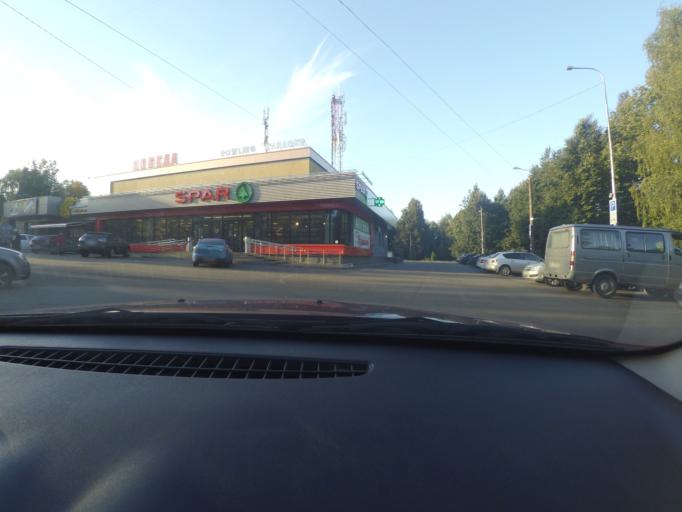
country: RU
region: Nizjnij Novgorod
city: Nizhniy Novgorod
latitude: 56.2923
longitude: 44.0067
